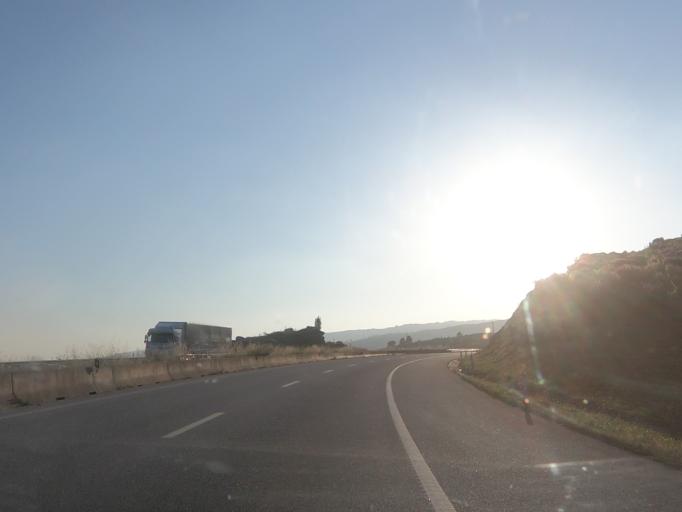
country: PT
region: Guarda
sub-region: Celorico da Beira
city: Celorico da Beira
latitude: 40.6345
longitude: -7.4509
